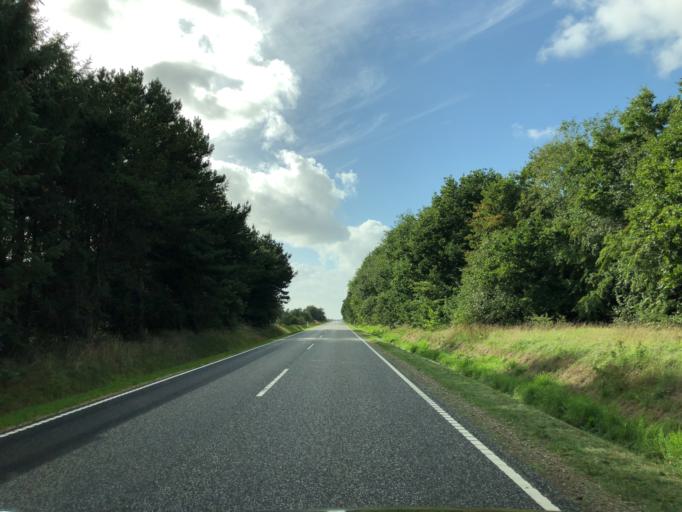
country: DK
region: Central Jutland
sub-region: Holstebro Kommune
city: Holstebro
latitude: 56.3704
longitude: 8.4876
